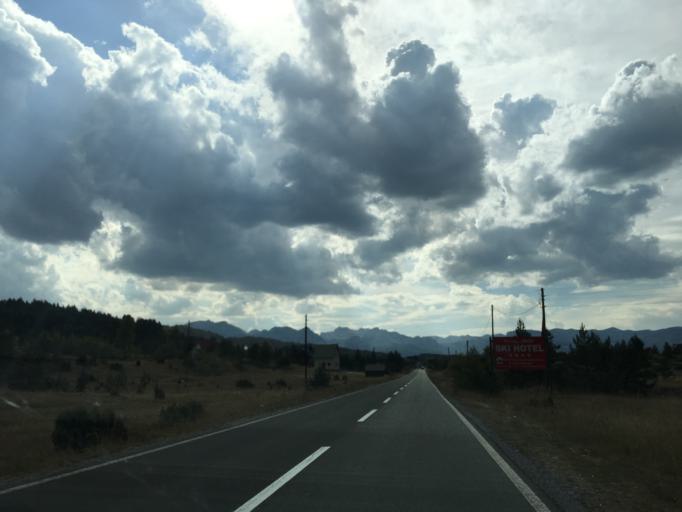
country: ME
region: Opstina Zabljak
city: Zabljak
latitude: 43.1655
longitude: 19.1812
